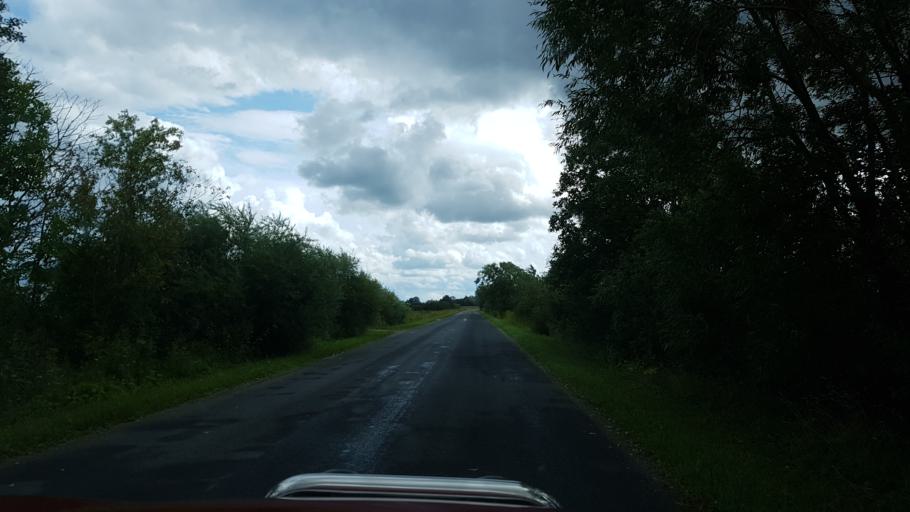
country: EE
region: Laeaene
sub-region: Lihula vald
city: Lihula
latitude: 58.7175
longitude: 23.9878
